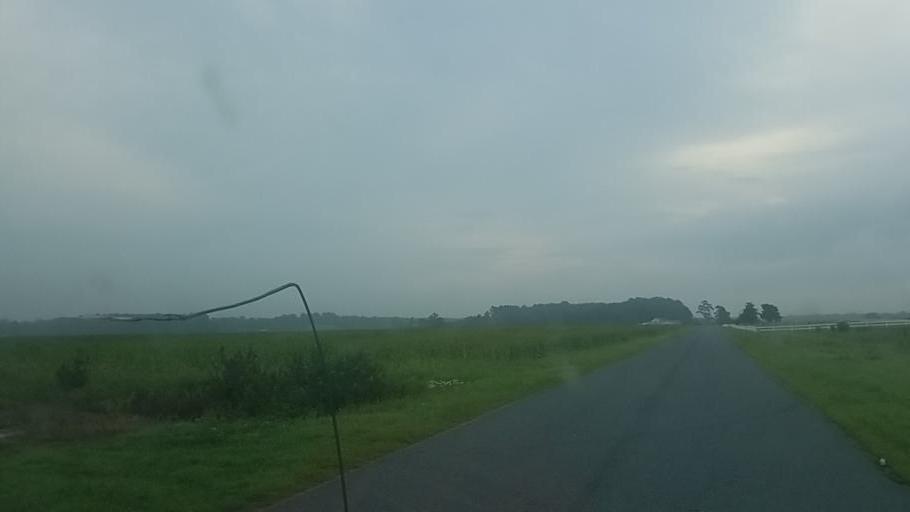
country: US
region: Maryland
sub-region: Wicomico County
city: Pittsville
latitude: 38.4521
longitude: -75.3628
